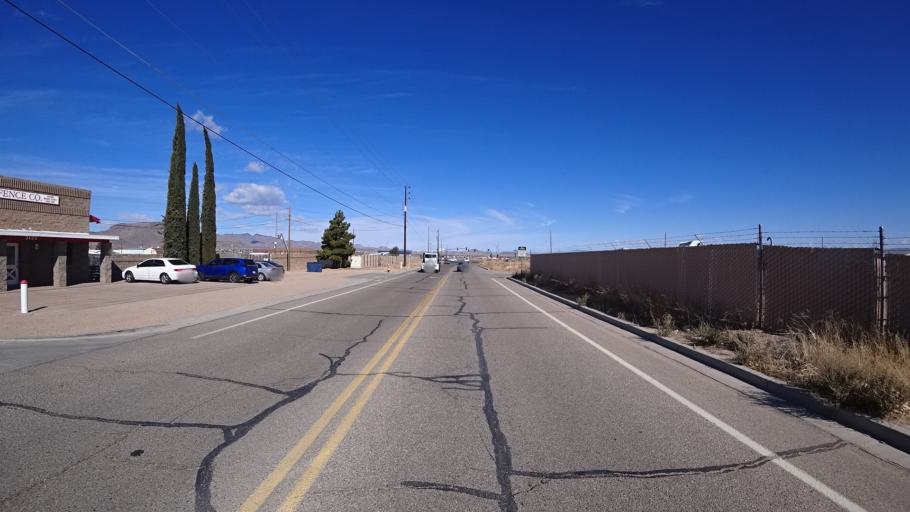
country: US
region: Arizona
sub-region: Mohave County
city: New Kingman-Butler
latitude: 35.2230
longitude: -114.0115
